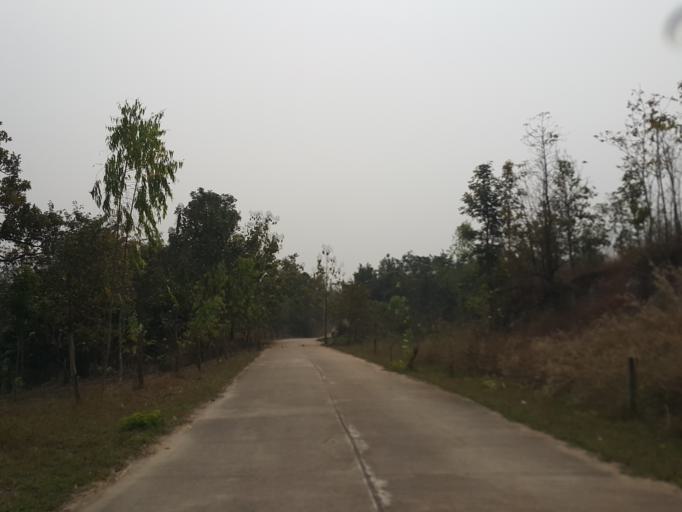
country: TH
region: Lampang
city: Thoen
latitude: 17.6330
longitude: 99.2567
